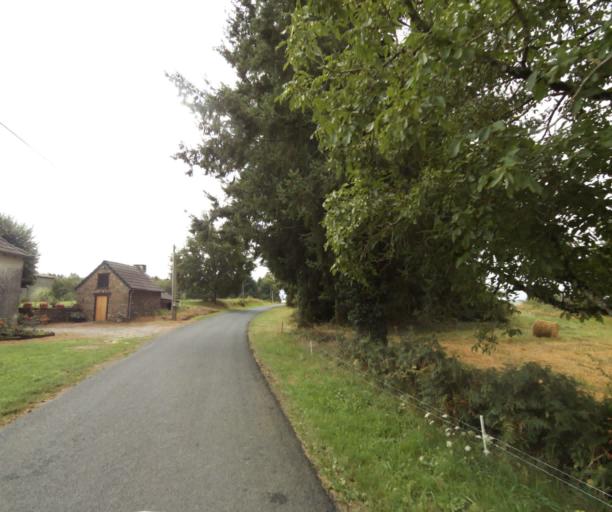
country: FR
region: Limousin
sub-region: Departement de la Correze
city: Sainte-Fortunade
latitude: 45.1695
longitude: 1.8033
